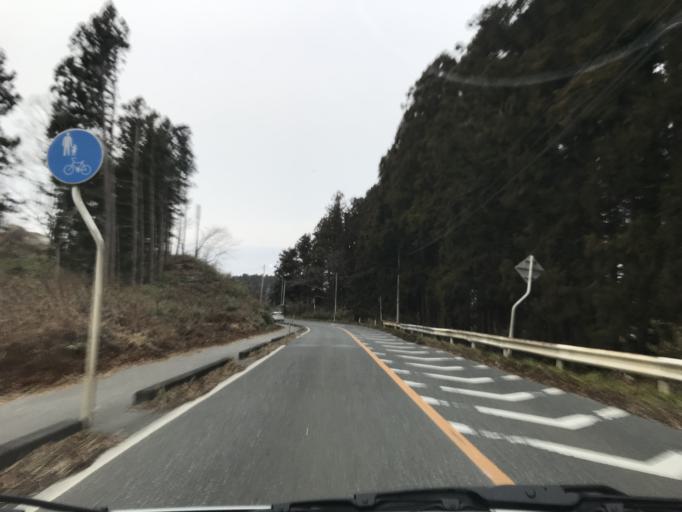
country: JP
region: Miyagi
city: Wakuya
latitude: 38.6947
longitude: 141.1514
